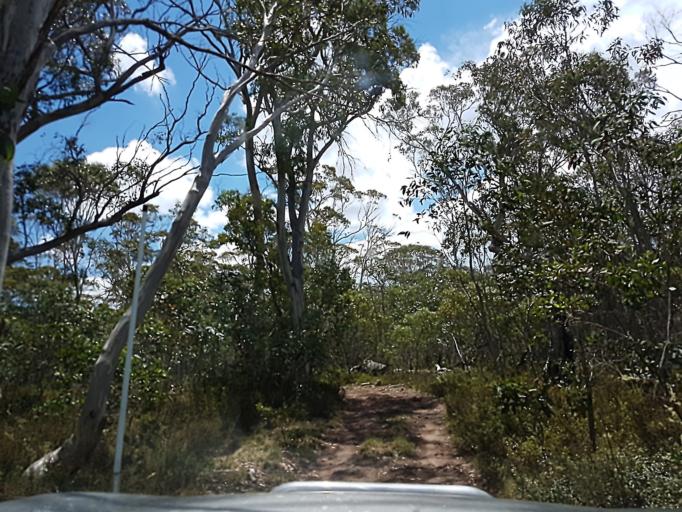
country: AU
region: New South Wales
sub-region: Snowy River
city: Jindabyne
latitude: -36.9184
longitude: 148.1324
